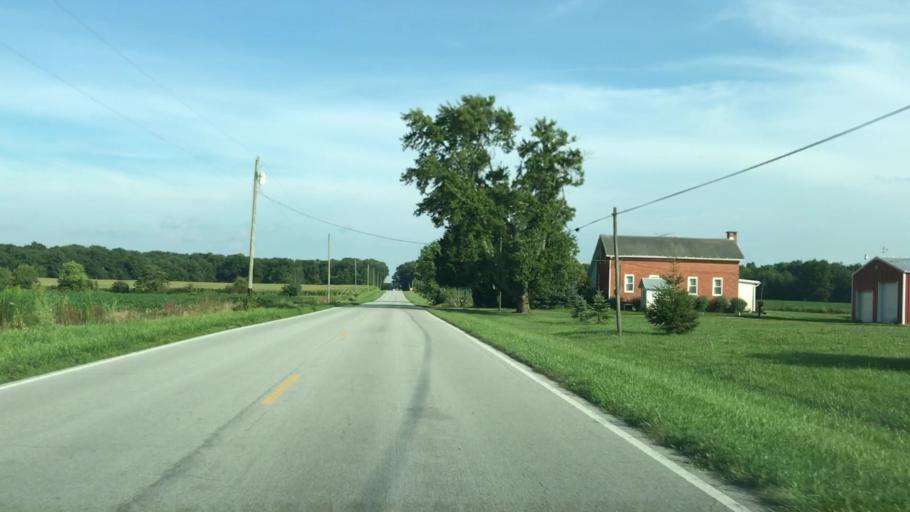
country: US
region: Ohio
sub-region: Union County
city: Marysville
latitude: 40.1981
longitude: -83.3419
